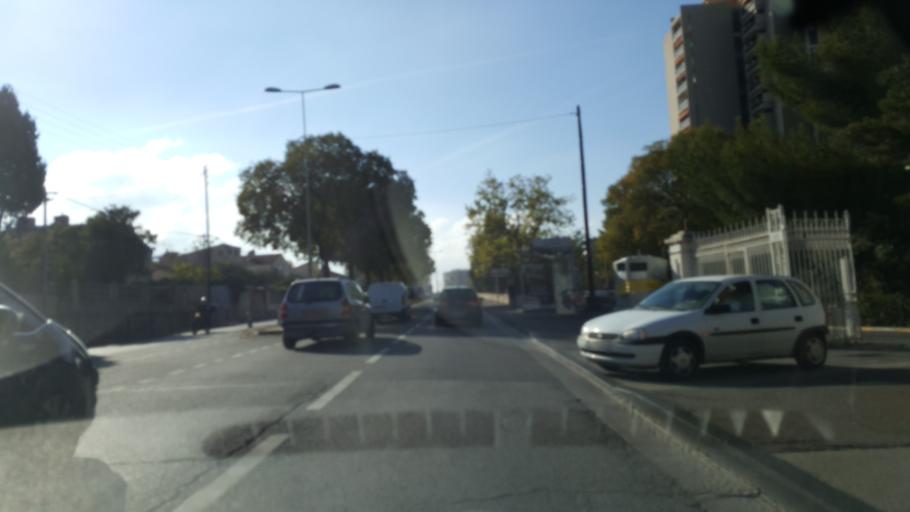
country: FR
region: Provence-Alpes-Cote d'Azur
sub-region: Departement des Bouches-du-Rhone
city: Marseille 10
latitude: 43.2710
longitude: 5.4252
